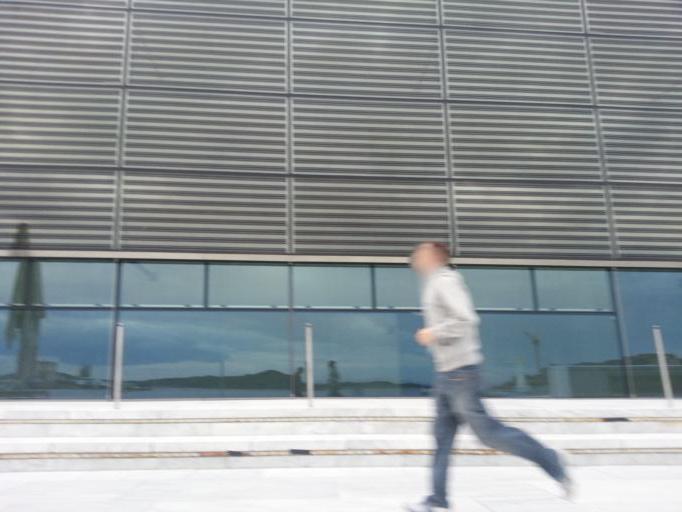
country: NO
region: Oslo
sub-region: Oslo
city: Oslo
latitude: 59.9071
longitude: 10.7522
